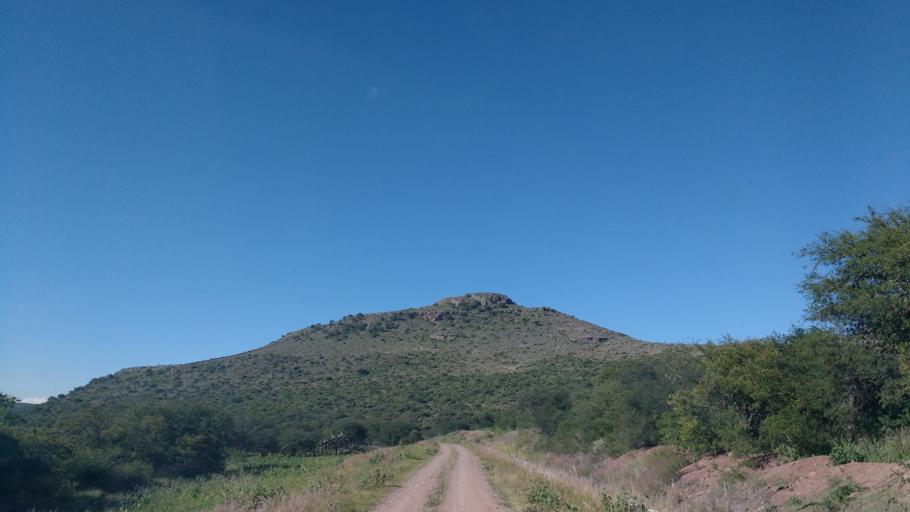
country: MX
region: Hidalgo
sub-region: Tezontepec de Aldama
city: Tenango
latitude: 20.2448
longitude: -99.2773
